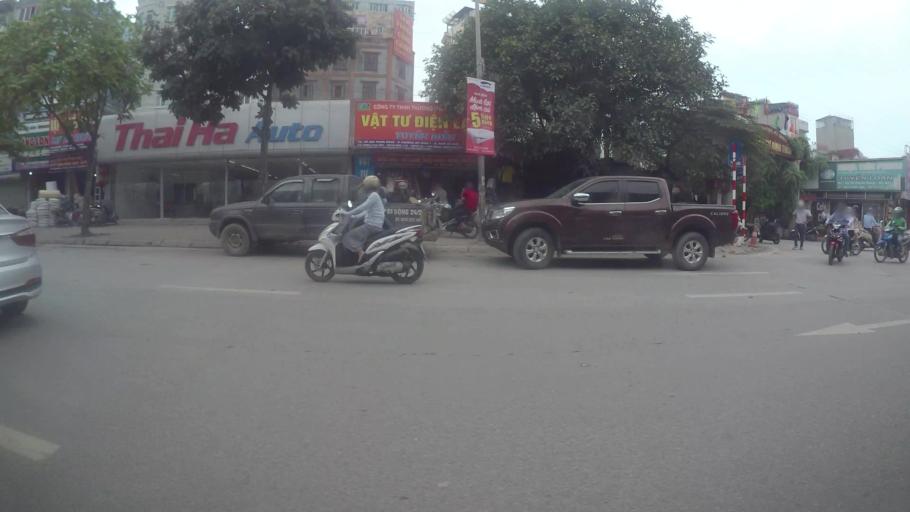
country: VN
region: Ha Noi
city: Cau Dien
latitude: 21.0213
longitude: 105.7791
